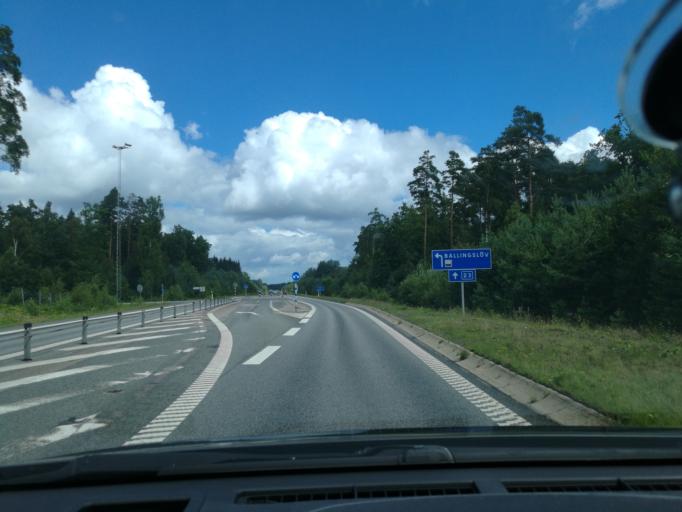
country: SE
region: Skane
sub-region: Hassleholms Kommun
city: Hassleholm
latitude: 56.1986
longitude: 13.8553
